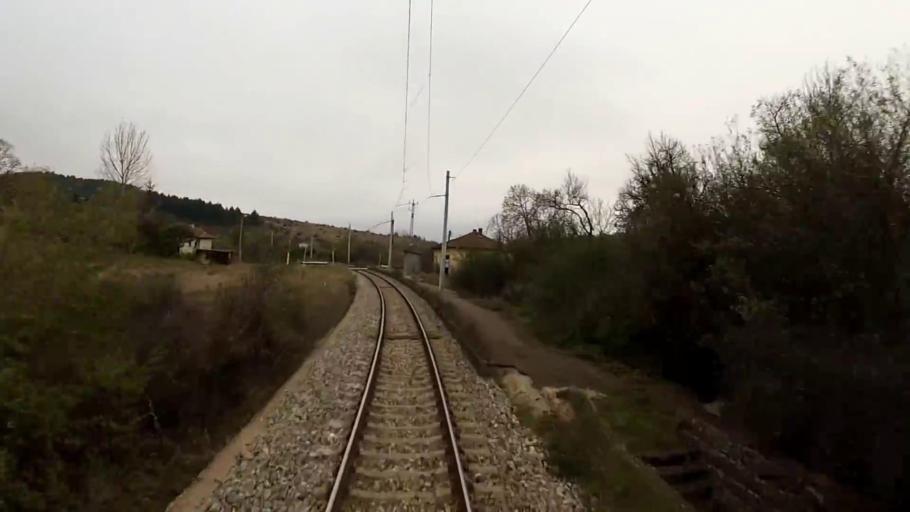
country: BG
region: Sofiya
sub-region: Obshtina Dragoman
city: Dragoman
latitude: 42.9355
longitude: 22.9032
